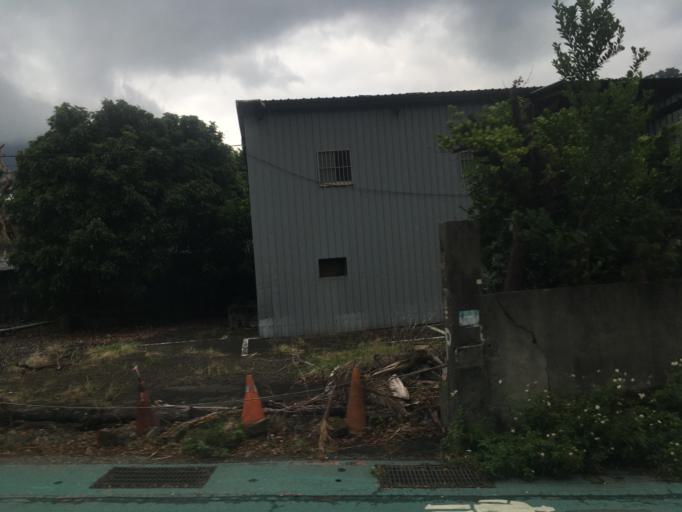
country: TW
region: Taipei
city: Taipei
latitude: 25.1377
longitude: 121.5282
